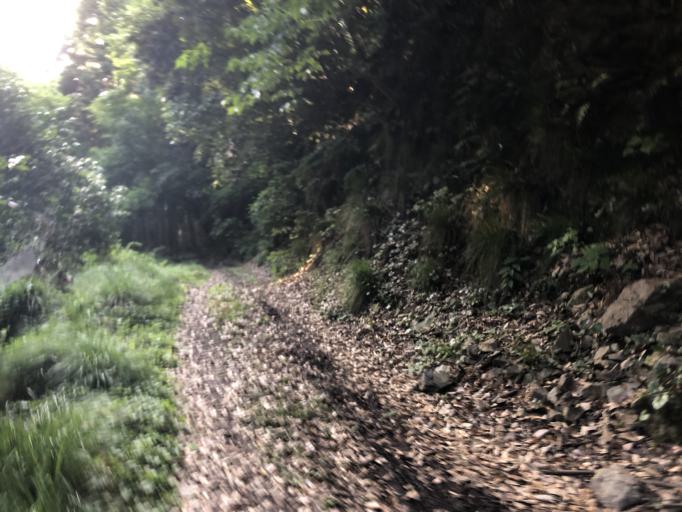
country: JP
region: Kyoto
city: Kameoka
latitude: 34.9876
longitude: 135.6233
